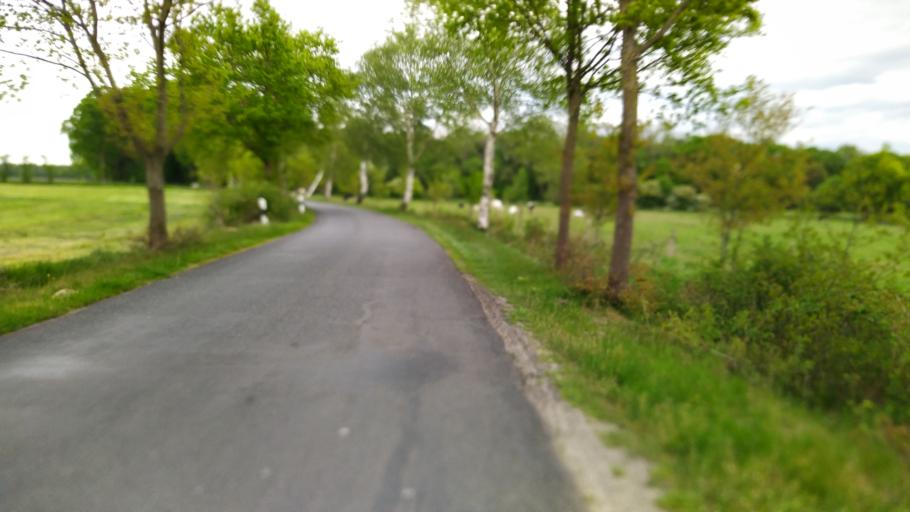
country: DE
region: Lower Saxony
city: Farven
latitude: 53.4006
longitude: 9.3576
